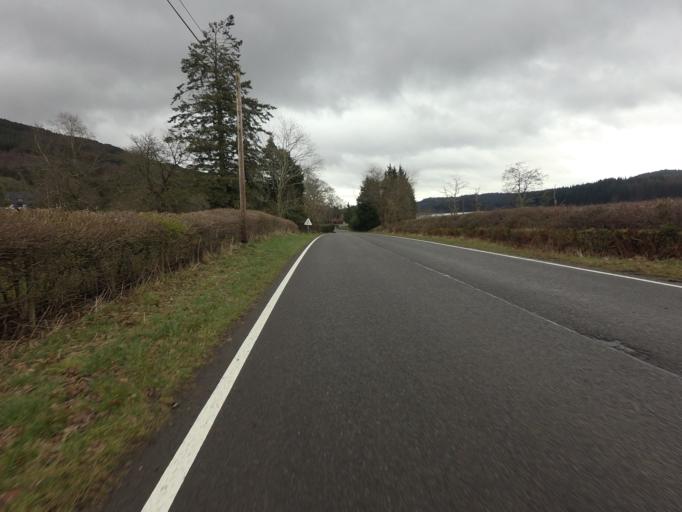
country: GB
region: Scotland
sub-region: Stirling
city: Killearn
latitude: 56.1881
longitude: -4.4832
